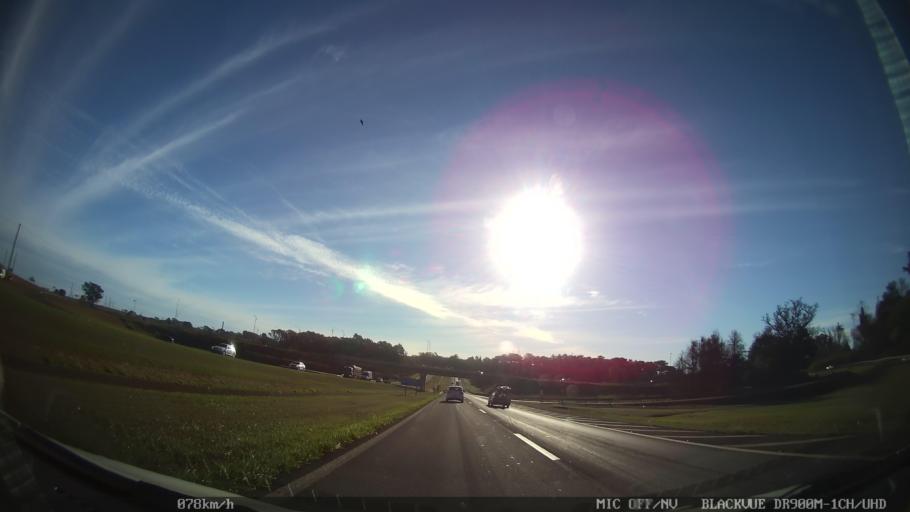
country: BR
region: Sao Paulo
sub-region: Sao Jose Do Rio Preto
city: Sao Jose do Rio Preto
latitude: -20.8190
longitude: -49.4333
